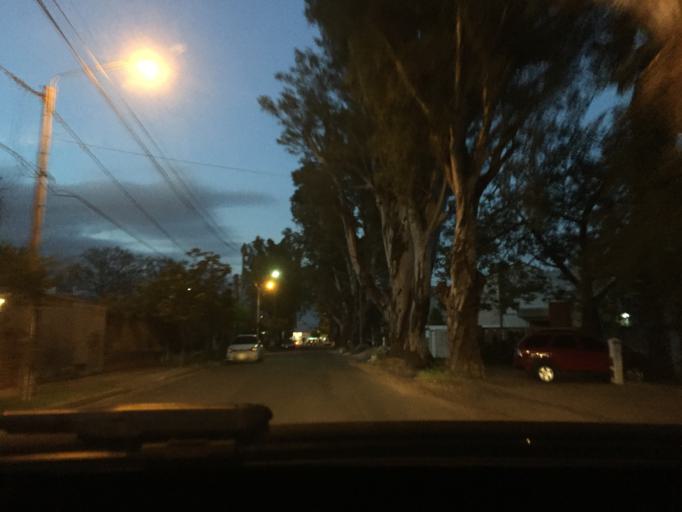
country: AR
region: Cordoba
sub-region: Departamento de Capital
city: Cordoba
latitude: -31.3743
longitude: -64.2247
